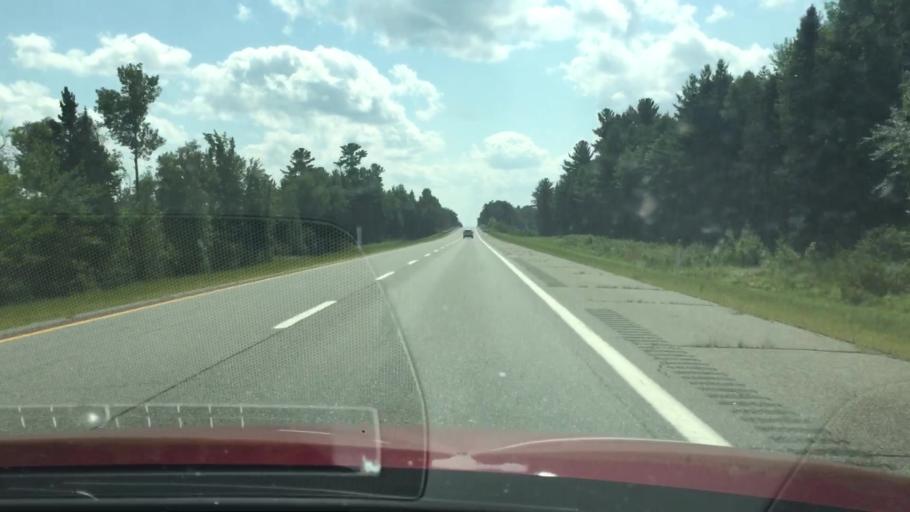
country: US
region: Maine
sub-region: Penobscot County
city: Lincoln
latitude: 45.4008
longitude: -68.5993
